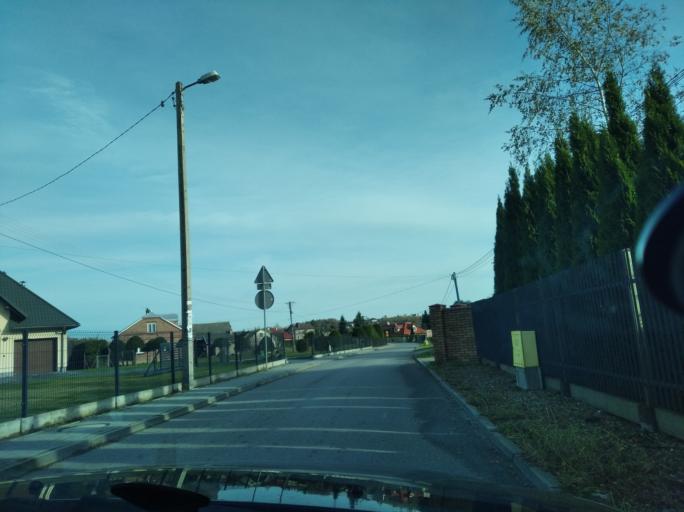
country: PL
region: Subcarpathian Voivodeship
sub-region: Powiat rzeszowski
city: Krasne
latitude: 50.0086
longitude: 22.0922
